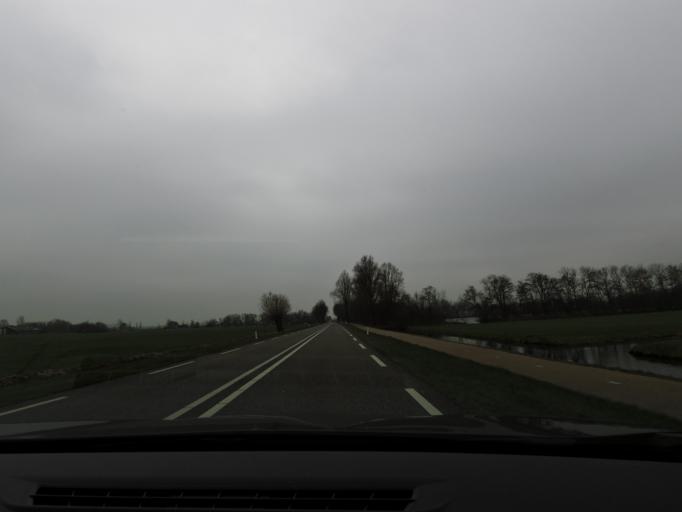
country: NL
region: Utrecht
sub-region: Gemeente Woerden
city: Woerden
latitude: 52.1344
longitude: 4.9121
